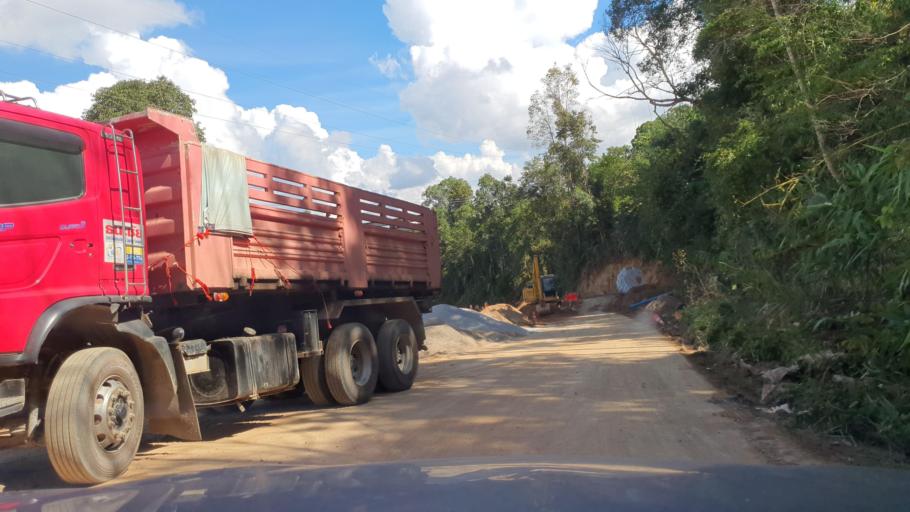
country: TH
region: Chiang Mai
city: Phrao
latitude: 19.3116
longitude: 99.3337
